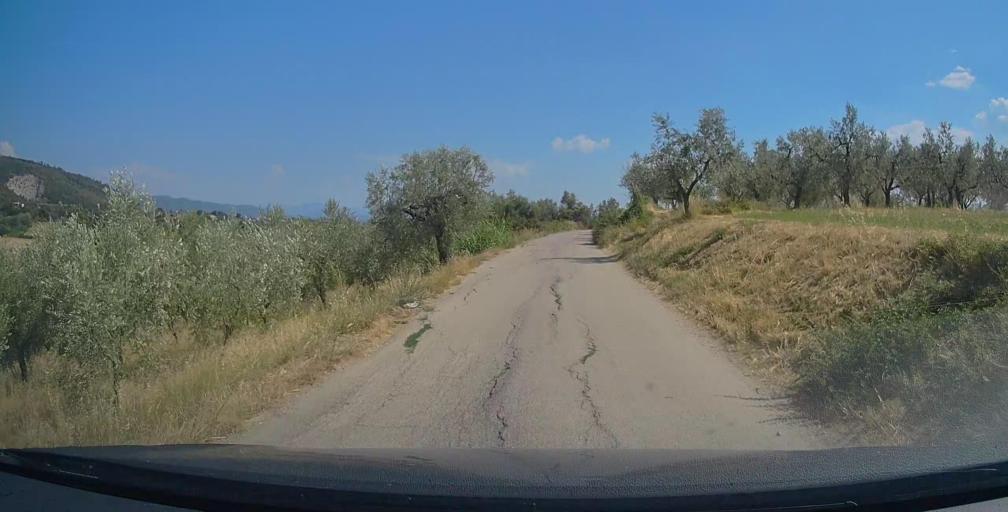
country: IT
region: Umbria
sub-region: Provincia di Terni
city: Calvi dell'Umbria
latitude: 42.3846
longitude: 12.5687
